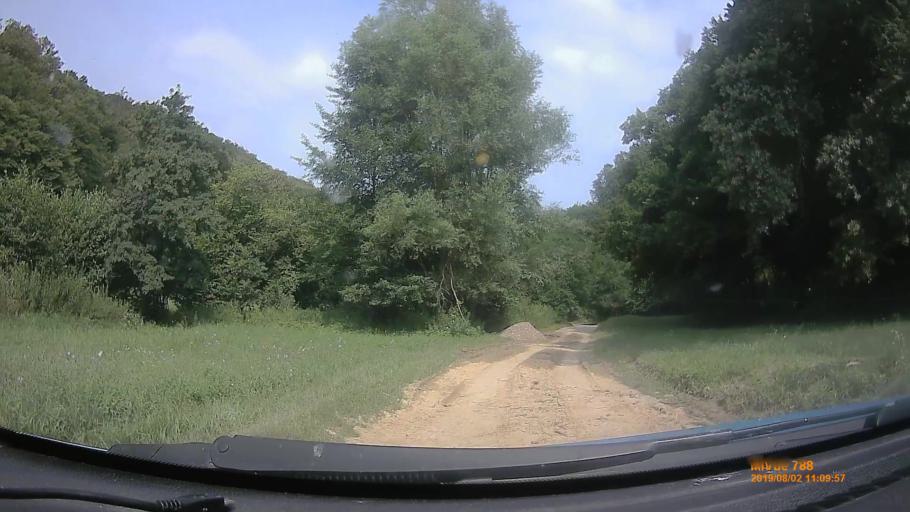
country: HU
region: Baranya
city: Buekkoesd
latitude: 46.1035
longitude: 17.9383
